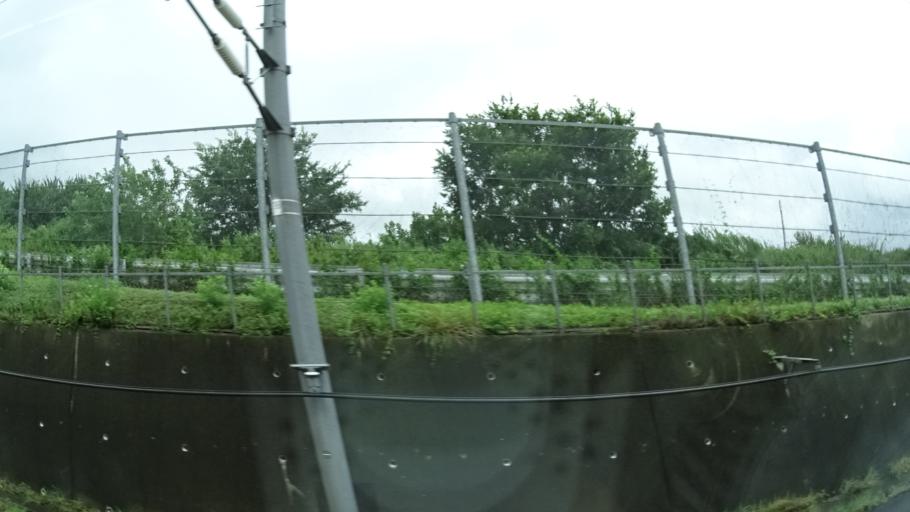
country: JP
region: Gunma
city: Annaka
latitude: 36.3781
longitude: 138.9339
